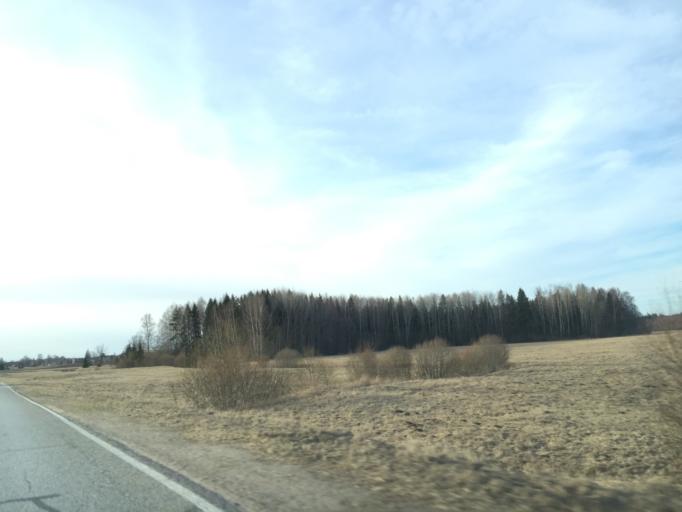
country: LV
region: Krimulda
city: Ragana
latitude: 57.1708
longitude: 24.7336
